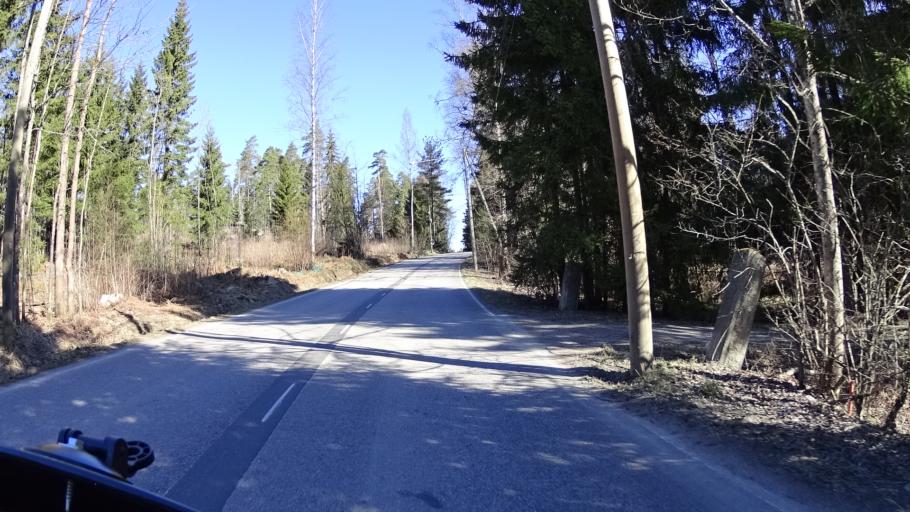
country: FI
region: Uusimaa
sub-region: Helsinki
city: Espoo
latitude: 60.2521
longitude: 24.6534
